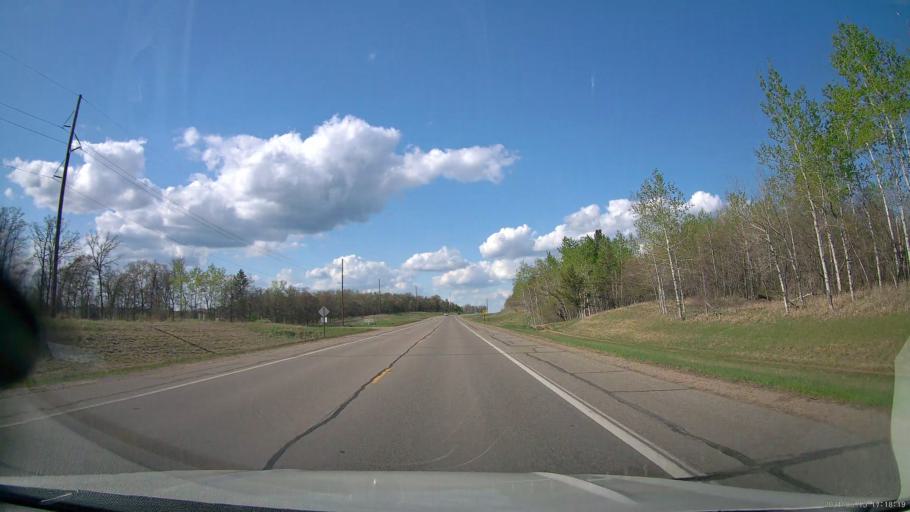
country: US
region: Minnesota
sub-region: Hubbard County
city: Park Rapids
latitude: 46.9595
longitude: -95.0184
